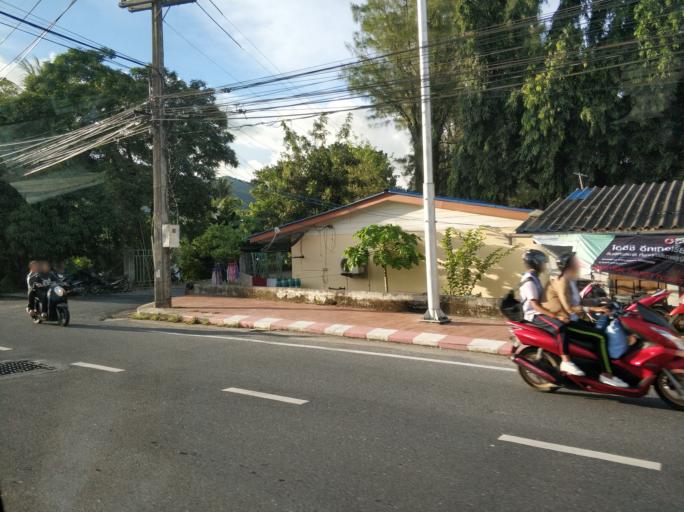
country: TH
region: Phuket
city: Kathu
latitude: 7.9019
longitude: 98.3385
